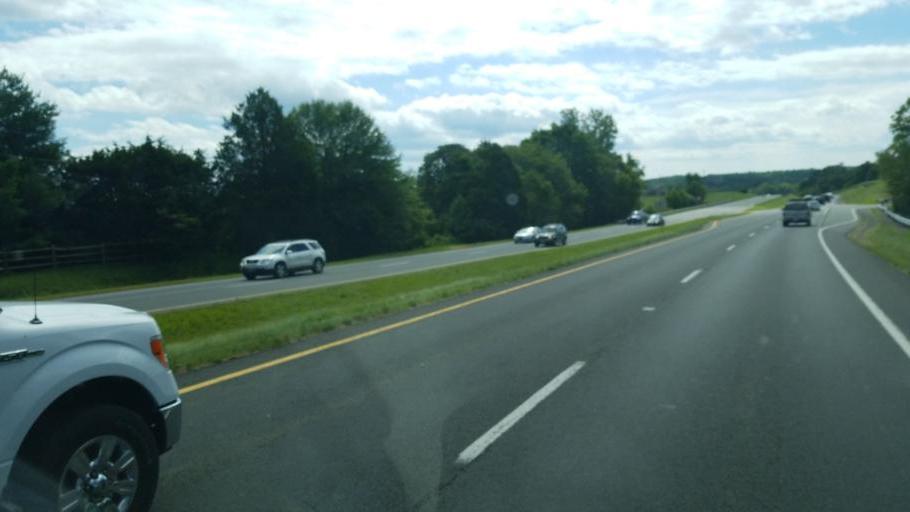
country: US
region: Virginia
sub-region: Fauquier County
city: Bealeton
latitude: 38.4391
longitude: -77.6422
